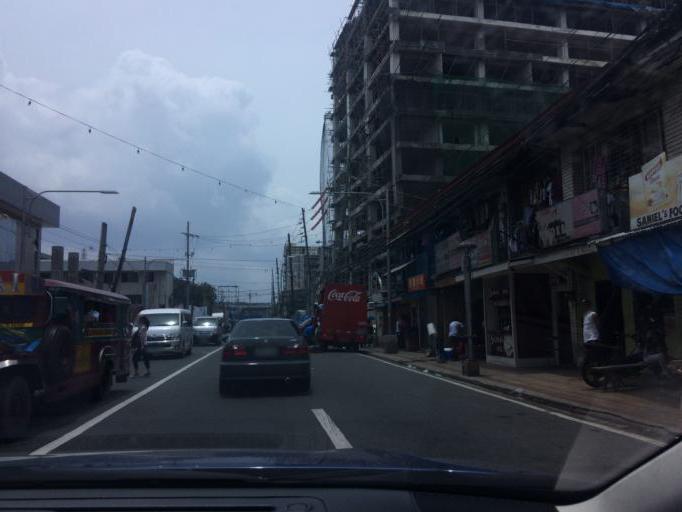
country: PH
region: Metro Manila
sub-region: Makati City
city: Makati City
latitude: 14.5209
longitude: 120.9967
